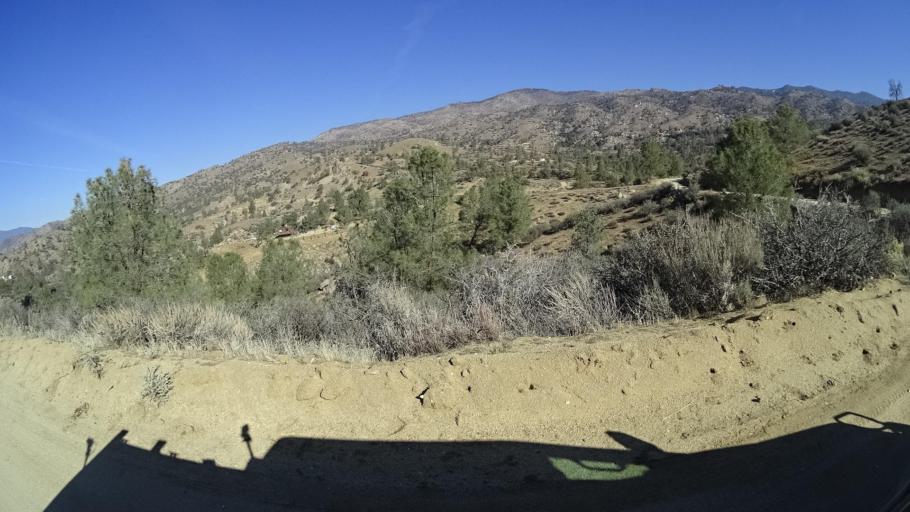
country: US
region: California
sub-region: Kern County
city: Bodfish
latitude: 35.3838
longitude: -118.4098
